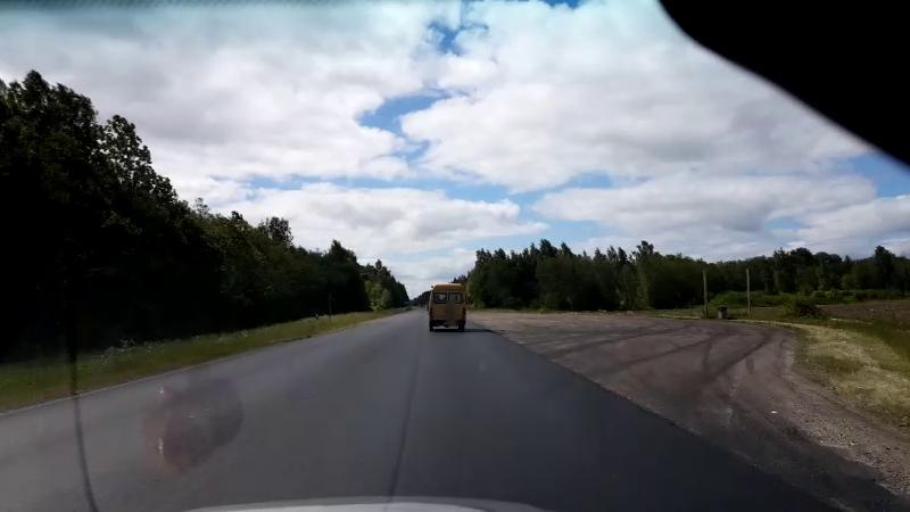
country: LV
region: Salacgrivas
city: Ainazi
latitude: 57.9649
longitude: 24.4465
